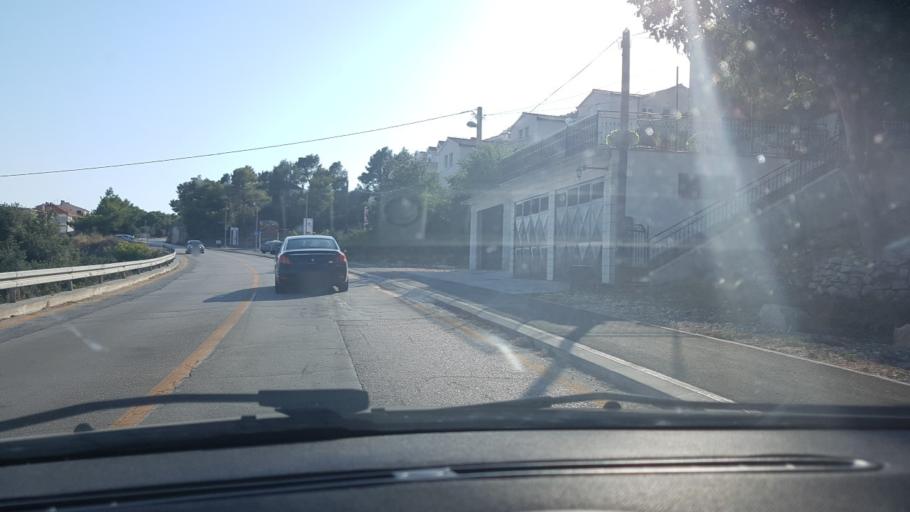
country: HR
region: Splitsko-Dalmatinska
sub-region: Grad Trogir
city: Trogir
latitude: 43.5163
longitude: 16.2139
